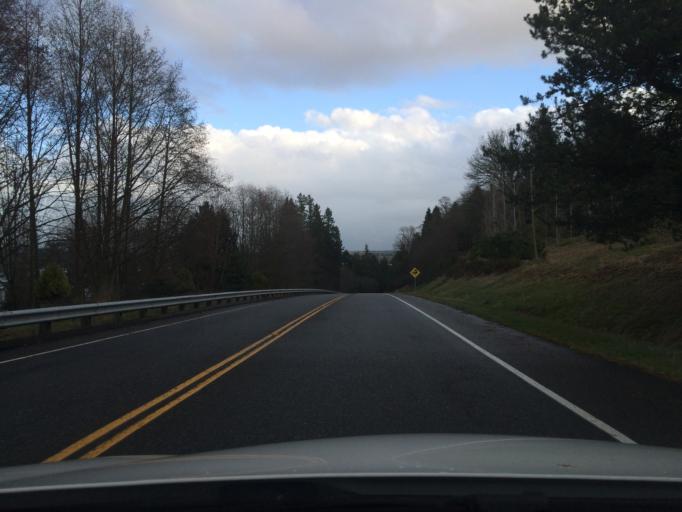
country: US
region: Washington
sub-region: Whatcom County
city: Blaine
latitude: 48.9652
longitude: -122.7775
